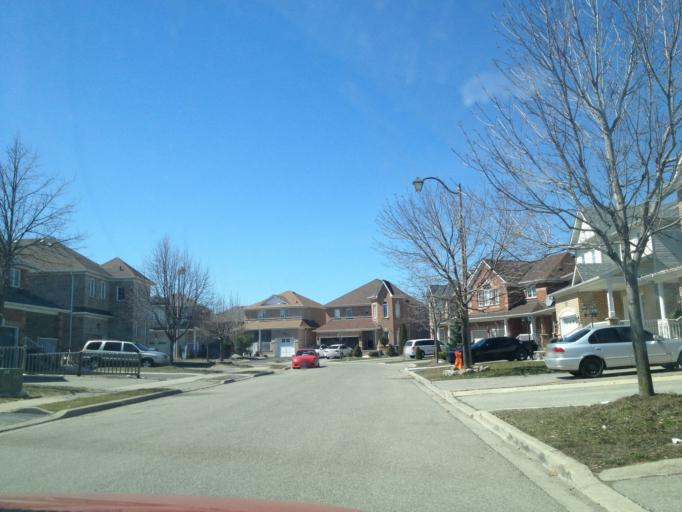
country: CA
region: Ontario
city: Brampton
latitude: 43.6851
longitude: -79.8119
